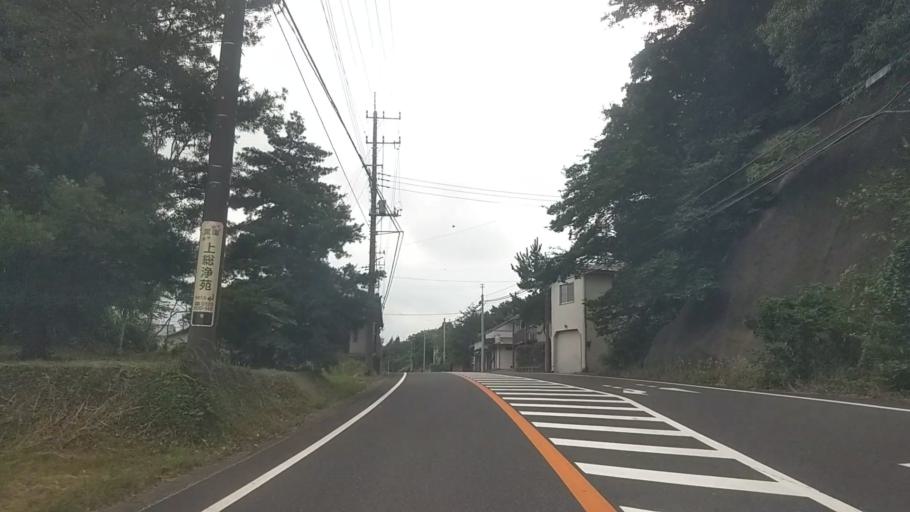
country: JP
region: Chiba
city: Kawaguchi
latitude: 35.2276
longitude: 140.0748
